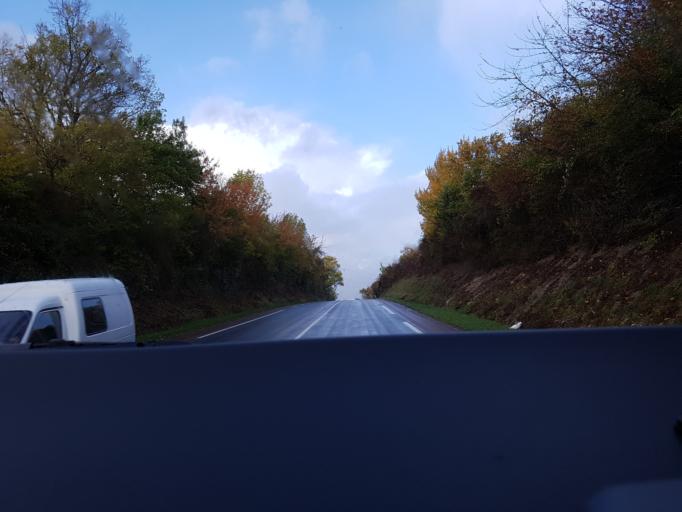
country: FR
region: Poitou-Charentes
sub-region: Departement de la Charente-Maritime
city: Les Gonds
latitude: 45.6777
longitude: -0.6057
